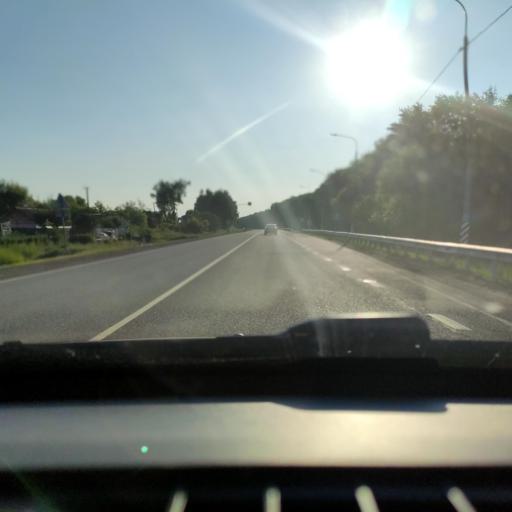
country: RU
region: Voronezj
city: Kashirskoye
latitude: 51.4587
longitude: 39.8003
